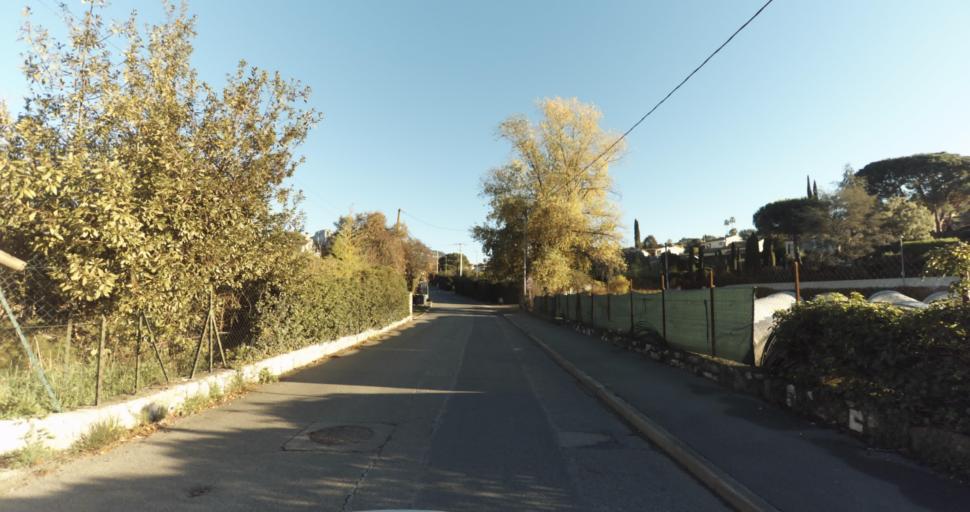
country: FR
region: Provence-Alpes-Cote d'Azur
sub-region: Departement des Alpes-Maritimes
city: Vence
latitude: 43.7141
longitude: 7.1293
